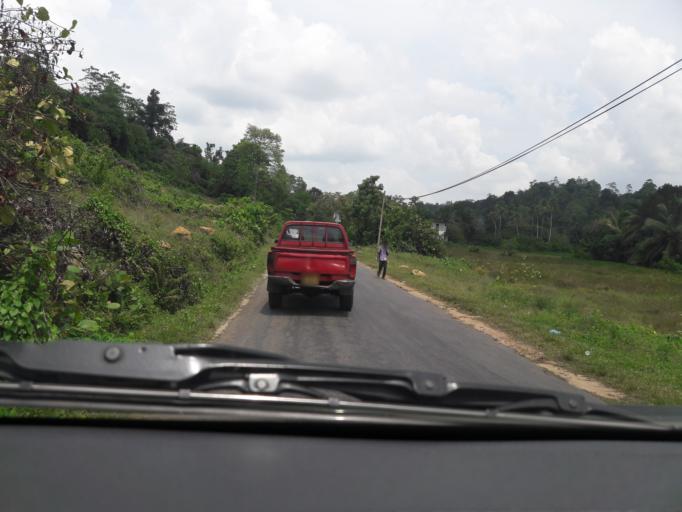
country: LK
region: Southern
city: Hikkaduwa
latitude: 6.2466
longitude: 80.2689
